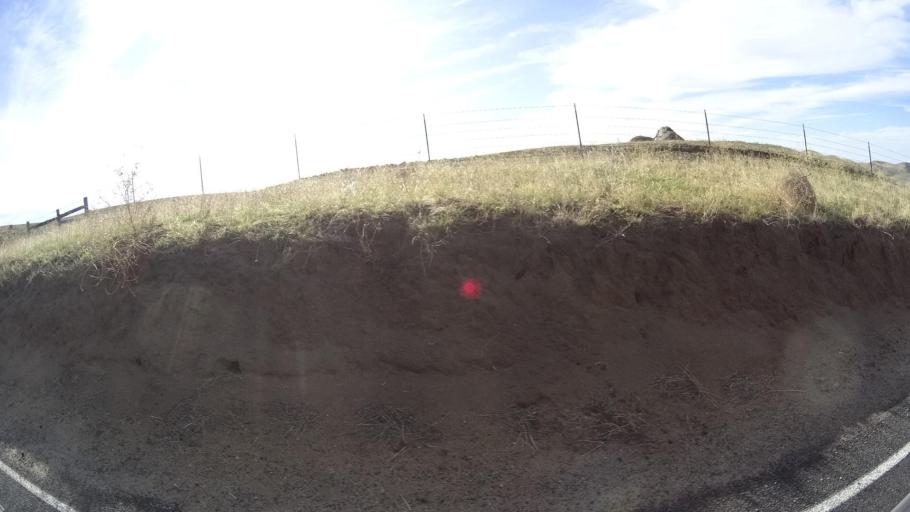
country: US
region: California
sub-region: Kern County
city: Oildale
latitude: 35.6120
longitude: -118.8657
